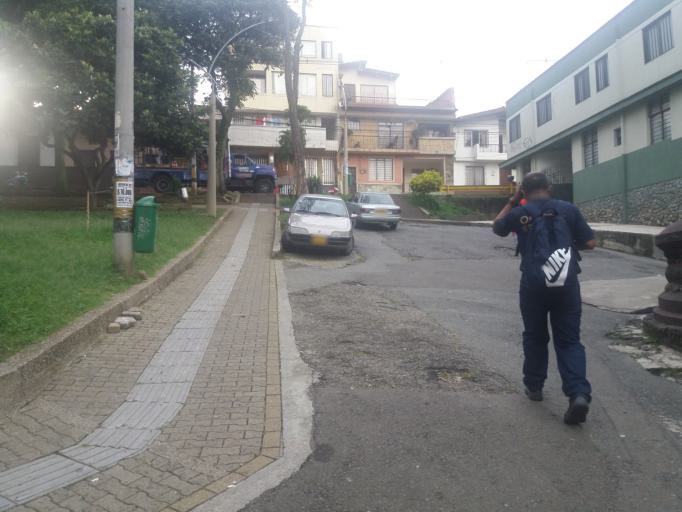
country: CO
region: Antioquia
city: Medellin
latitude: 6.2760
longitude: -75.5960
